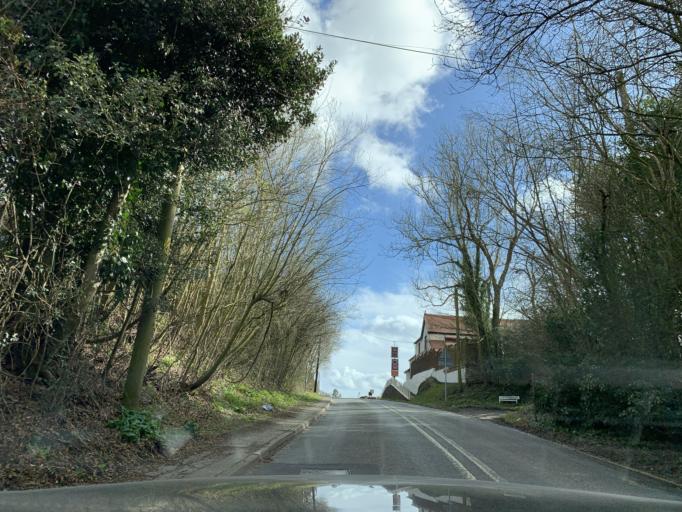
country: GB
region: England
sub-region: West Sussex
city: Crawley Down
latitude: 51.0985
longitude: -0.0841
